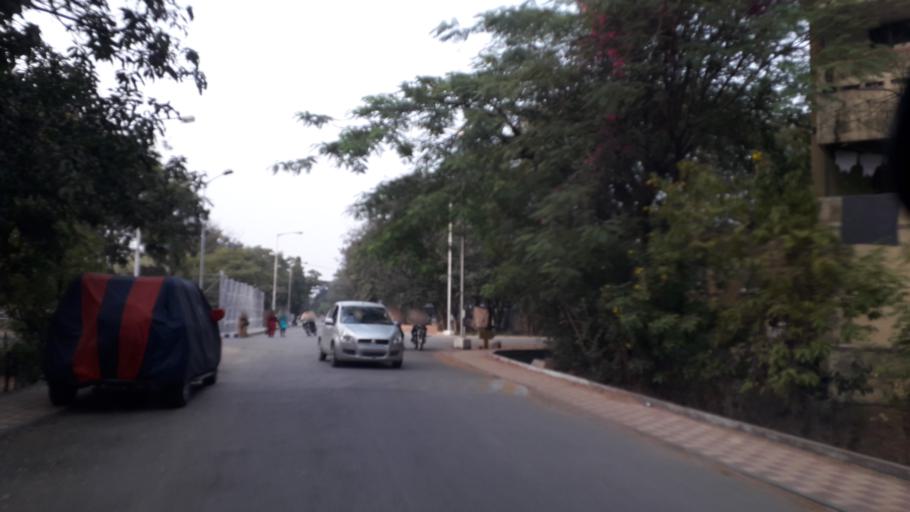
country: IN
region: Telangana
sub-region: Rangareddi
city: Singapur
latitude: 17.4684
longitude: 78.1630
